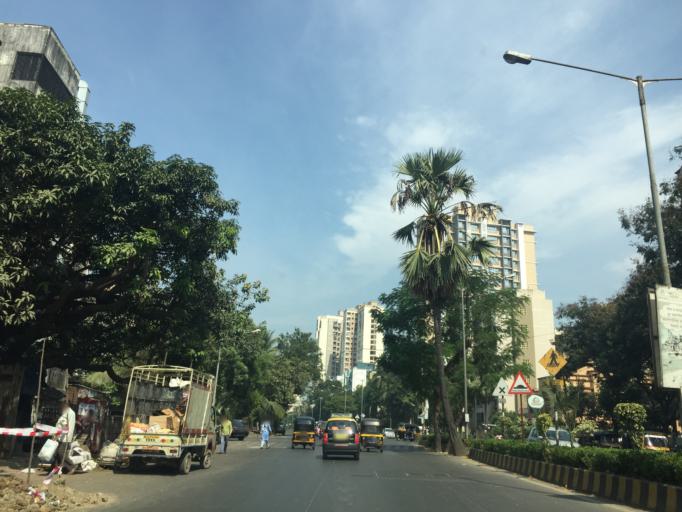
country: IN
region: Maharashtra
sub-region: Mumbai Suburban
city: Borivli
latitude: 19.2202
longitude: 72.8407
